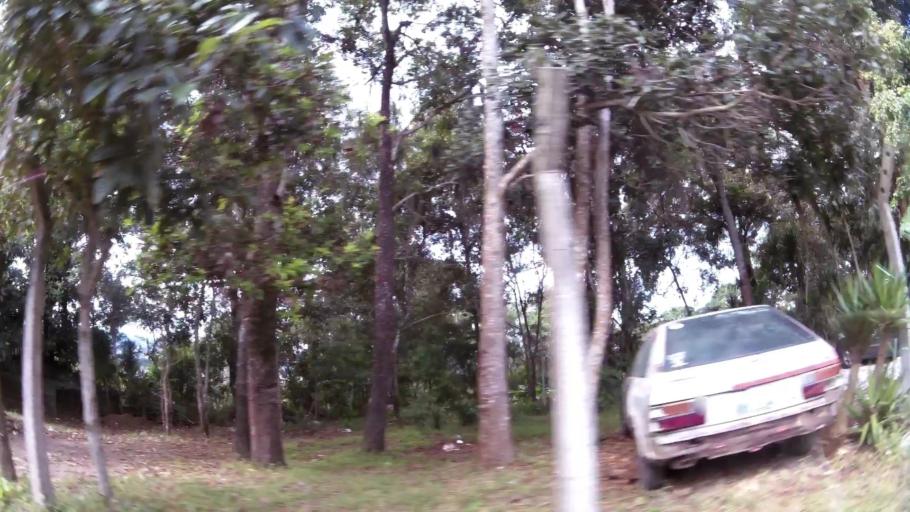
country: GT
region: Guatemala
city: Chinautla
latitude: 14.6881
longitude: -90.5508
